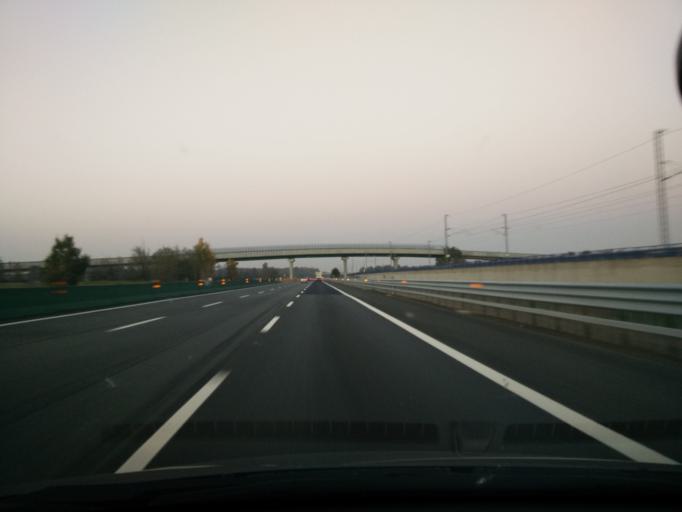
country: IT
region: Piedmont
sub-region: Provincia di Vercelli
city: Carisio
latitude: 45.4052
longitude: 8.1639
